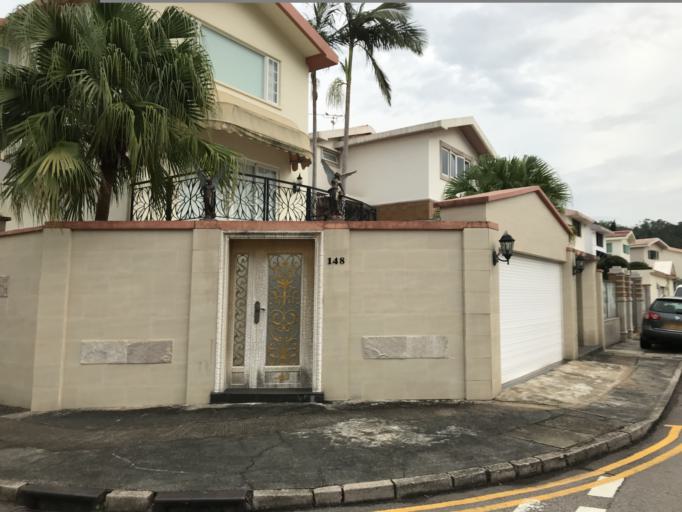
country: HK
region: Tai Po
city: Tai Po
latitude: 22.4648
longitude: 114.1550
